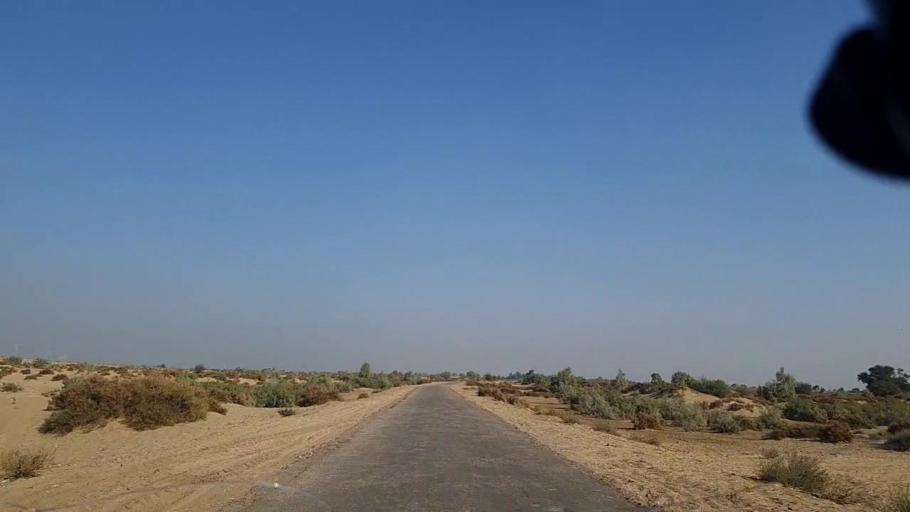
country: PK
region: Sindh
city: Khanpur
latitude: 27.6865
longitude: 69.4713
